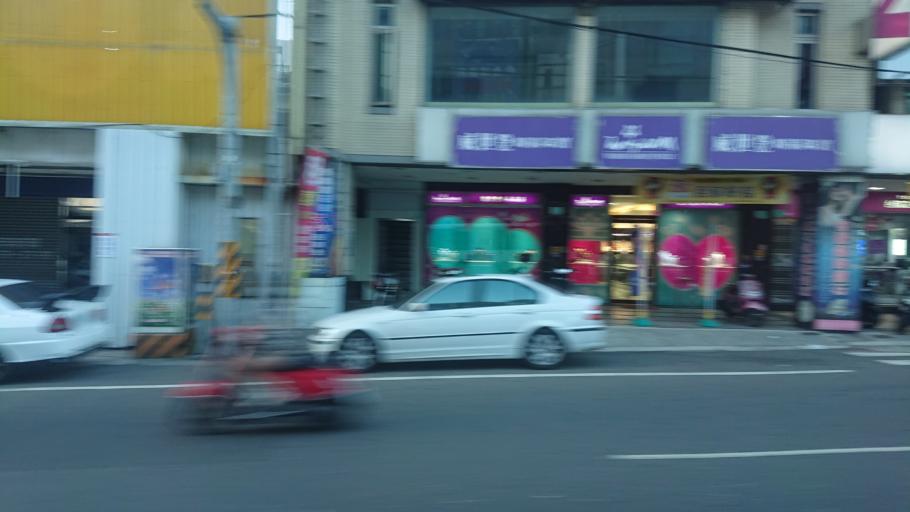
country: TW
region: Taiwan
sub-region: Tainan
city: Tainan
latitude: 23.0125
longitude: 120.2277
